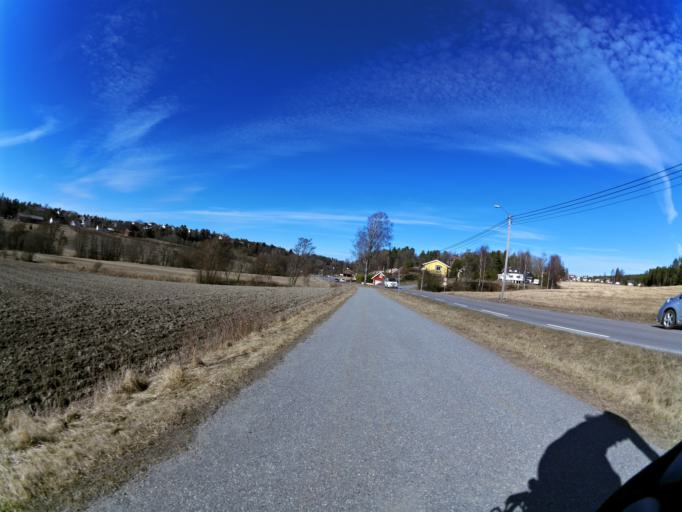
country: NO
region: Ostfold
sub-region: Fredrikstad
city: Fredrikstad
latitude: 59.2393
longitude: 10.9317
